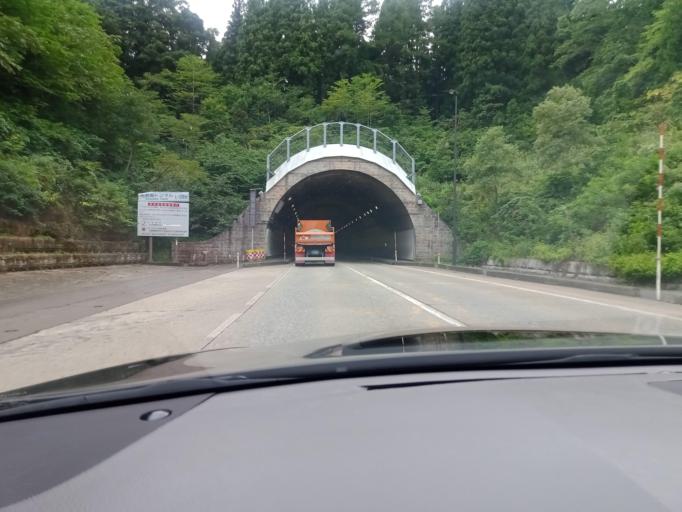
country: JP
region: Niigata
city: Arai
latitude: 36.8734
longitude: 138.2008
